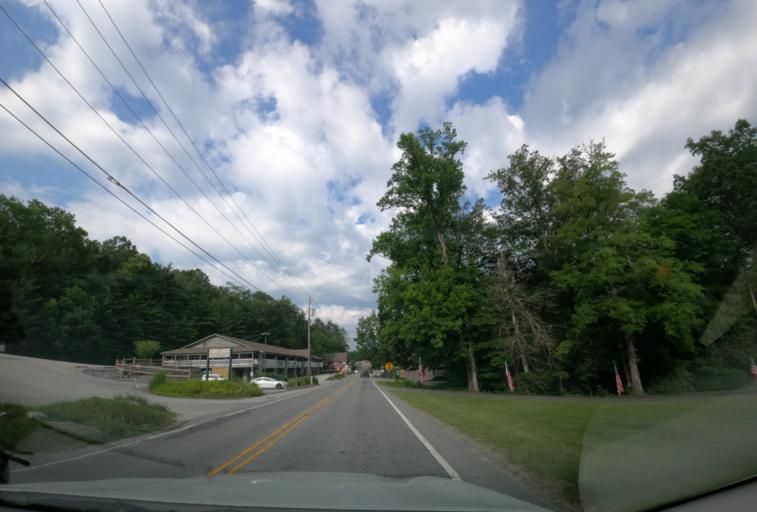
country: US
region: North Carolina
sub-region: Jackson County
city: Cullowhee
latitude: 35.1148
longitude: -83.0971
